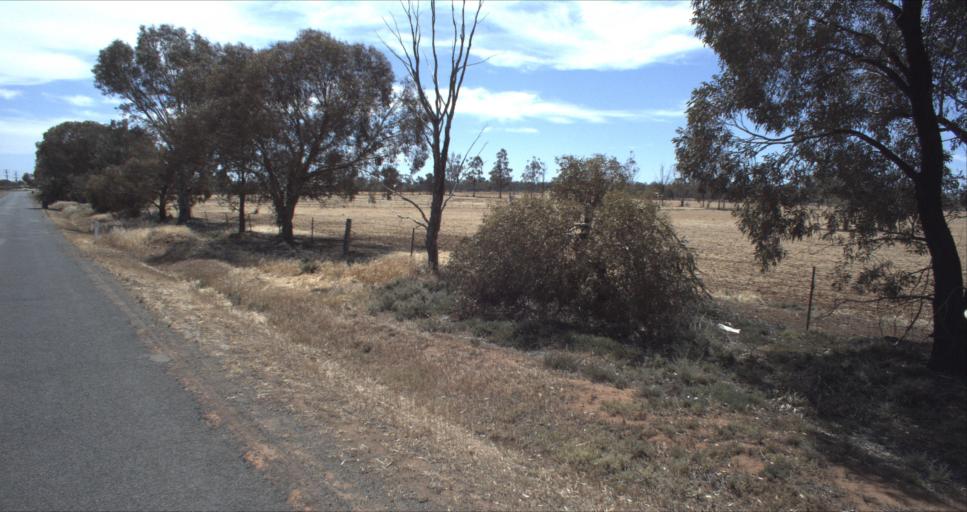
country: AU
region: New South Wales
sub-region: Leeton
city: Leeton
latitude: -34.5888
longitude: 146.4281
